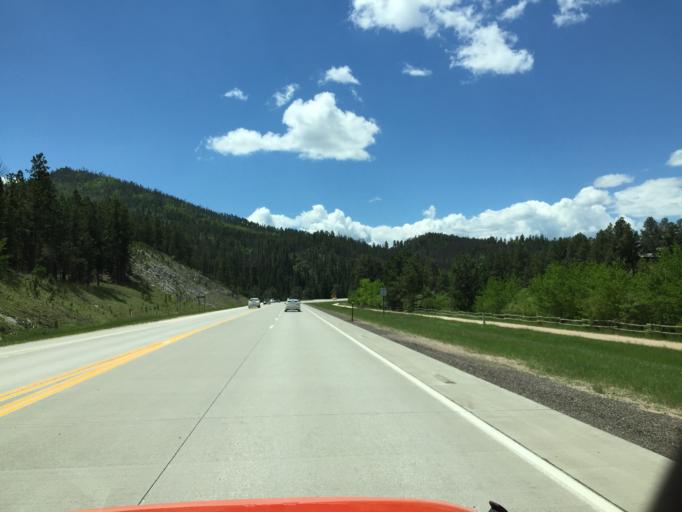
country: US
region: South Dakota
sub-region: Custer County
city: Custer
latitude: 43.8878
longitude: -103.5912
